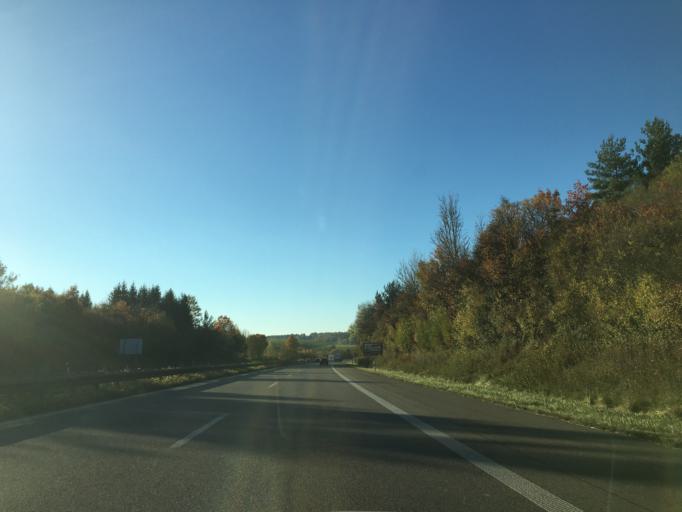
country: DE
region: Baden-Wuerttemberg
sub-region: Freiburg Region
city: Geisingen
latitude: 47.9277
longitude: 8.6422
